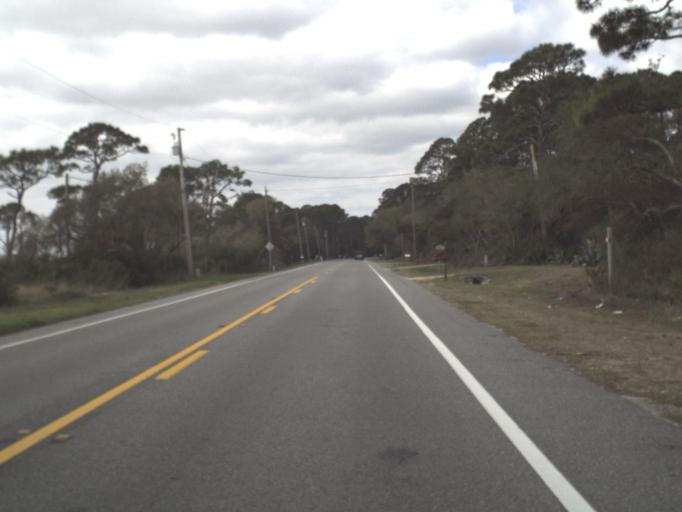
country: US
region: Florida
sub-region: Franklin County
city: Carrabelle
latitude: 29.8120
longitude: -84.7207
